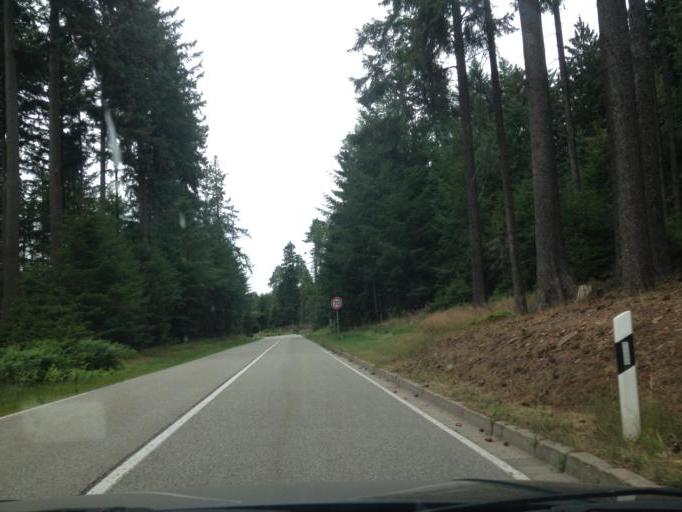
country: DE
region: Rheinland-Pfalz
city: Elmstein
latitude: 49.3120
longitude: 7.8630
